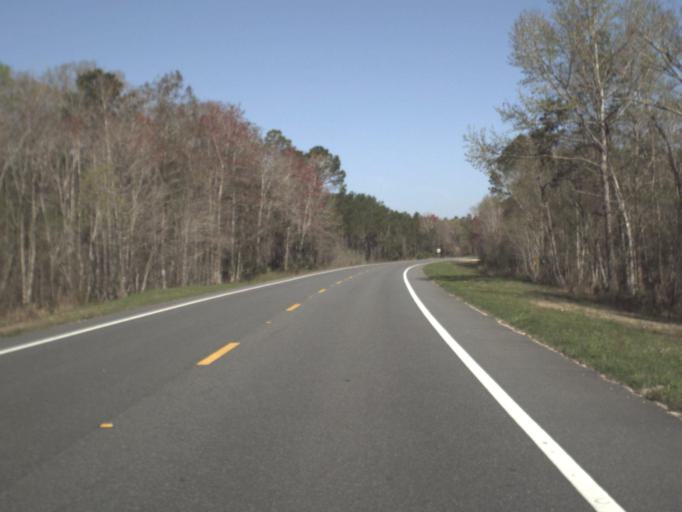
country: US
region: Florida
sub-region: Leon County
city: Woodville
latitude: 30.1606
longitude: -84.0017
